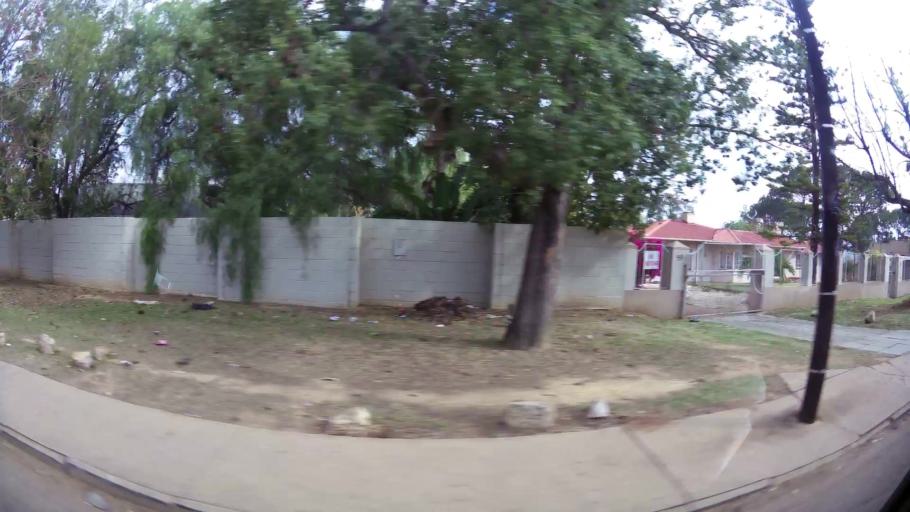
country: ZA
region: Eastern Cape
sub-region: Nelson Mandela Bay Metropolitan Municipality
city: Uitenhage
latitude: -33.7476
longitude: 25.4029
